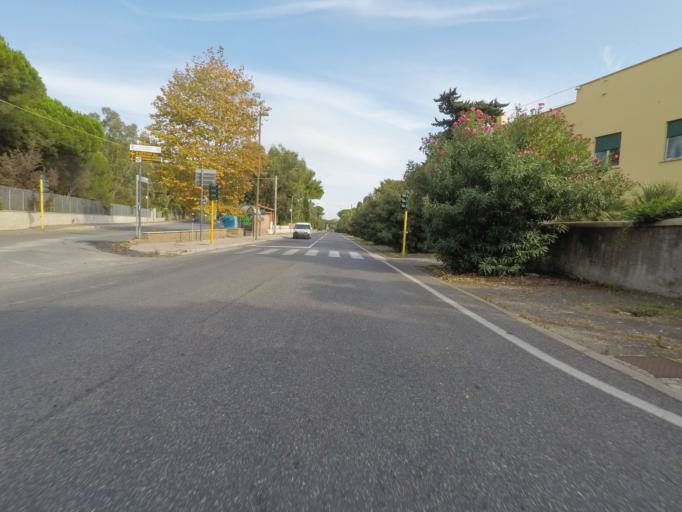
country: IT
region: Latium
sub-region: Citta metropolitana di Roma Capitale
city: Santa Marinella
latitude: 42.0324
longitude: 11.8410
